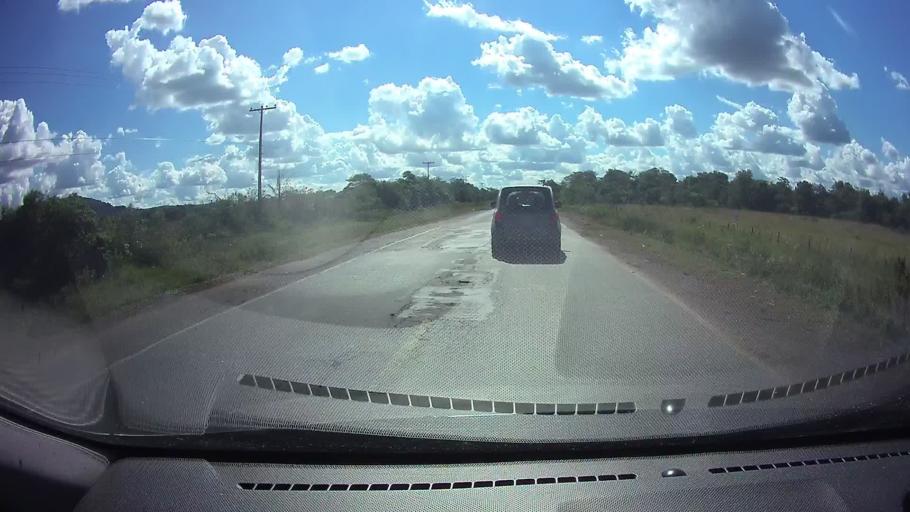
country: PY
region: Paraguari
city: La Colmena
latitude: -25.7518
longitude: -56.7839
